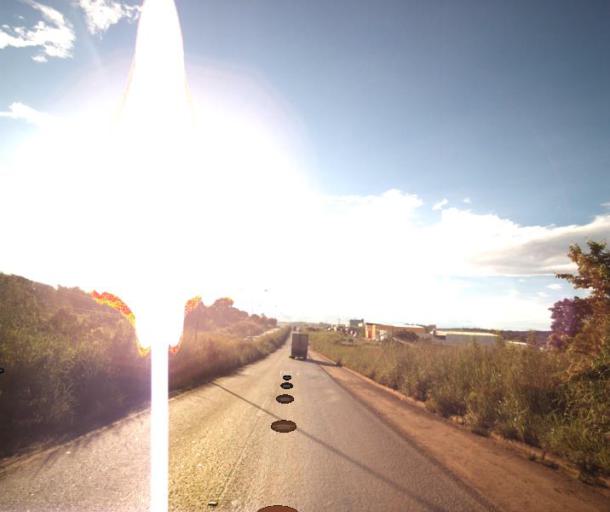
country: BR
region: Goias
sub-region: Anapolis
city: Anapolis
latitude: -16.2801
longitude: -48.9607
